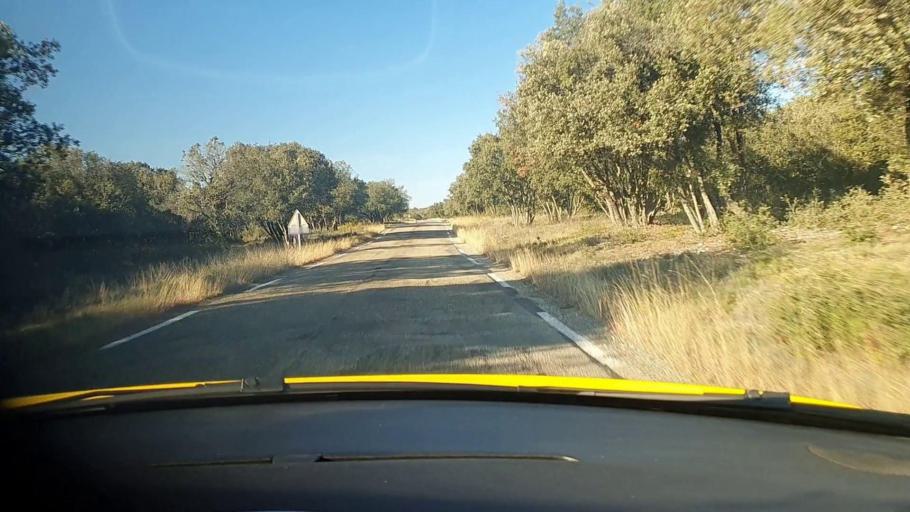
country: FR
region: Languedoc-Roussillon
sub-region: Departement du Gard
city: Goudargues
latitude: 44.1620
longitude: 4.3463
